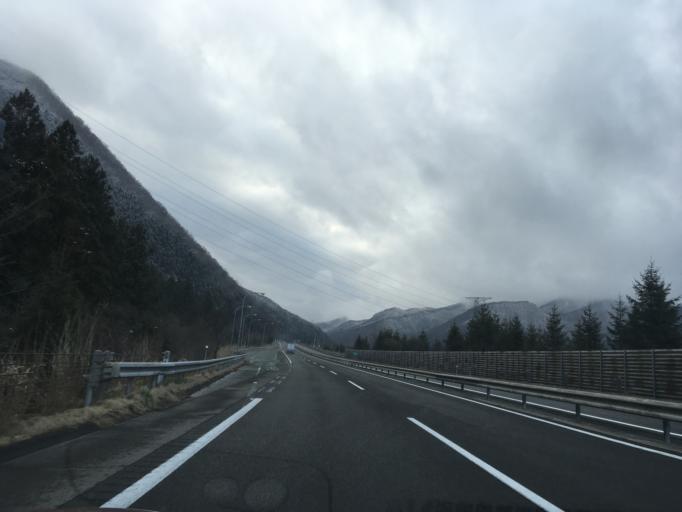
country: JP
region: Miyagi
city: Shiroishi
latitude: 38.1953
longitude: 140.5931
